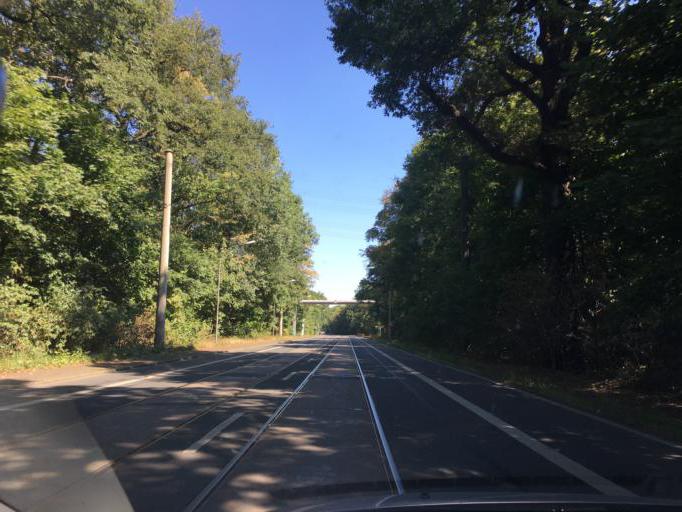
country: DE
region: Saxony
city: Markkleeberg
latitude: 51.2942
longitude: 12.3718
